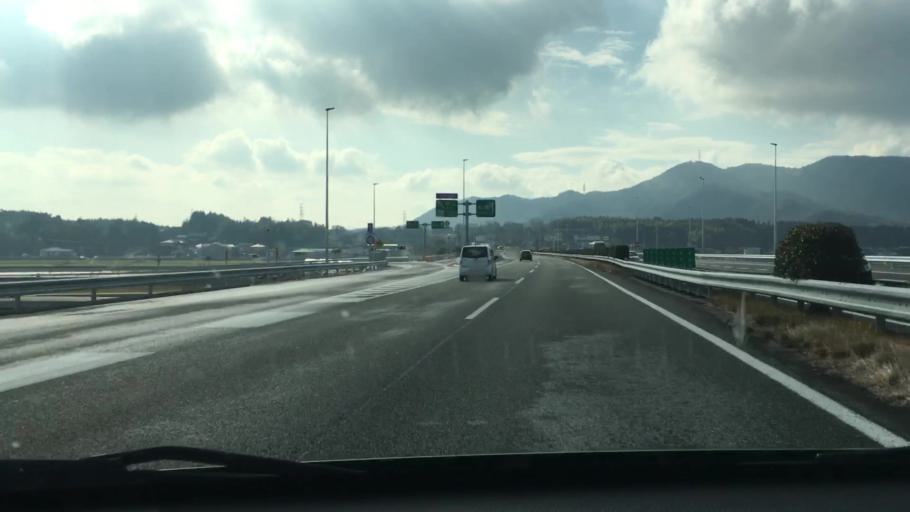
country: JP
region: Kumamoto
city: Uto
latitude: 32.6955
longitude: 130.7441
